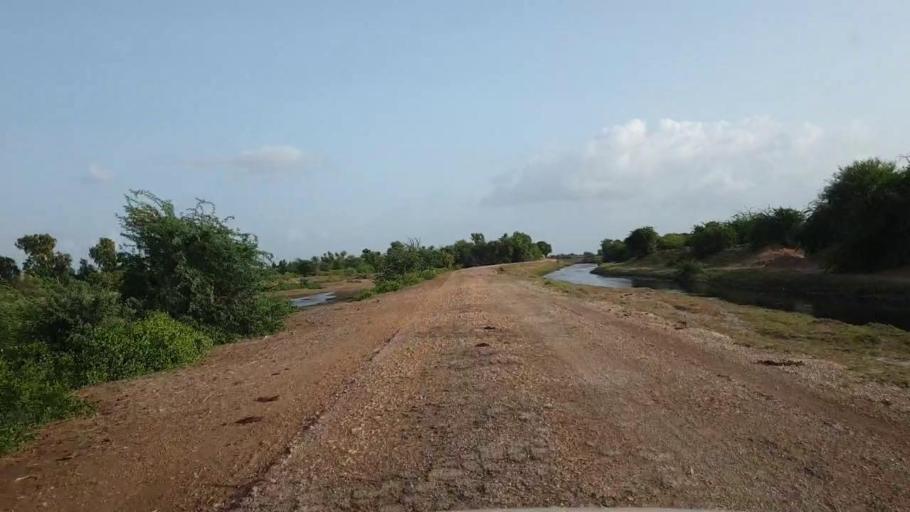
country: PK
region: Sindh
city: Kario
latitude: 24.8382
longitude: 68.6523
